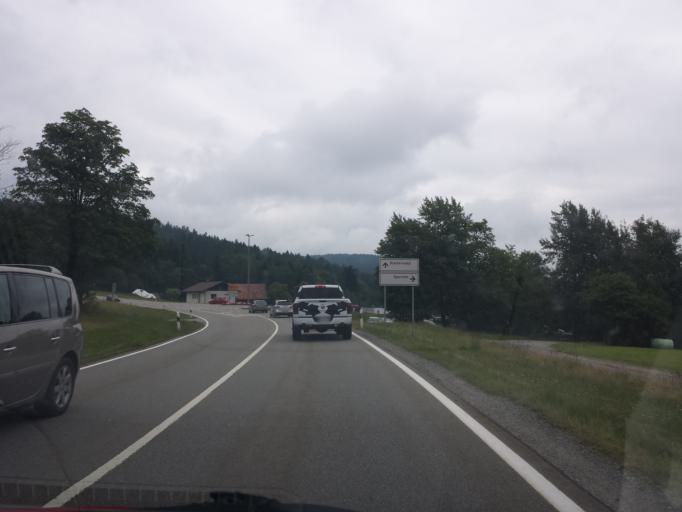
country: DE
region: Bavaria
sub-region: Lower Bavaria
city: Sankt Englmar
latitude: 49.0066
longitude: 12.8175
